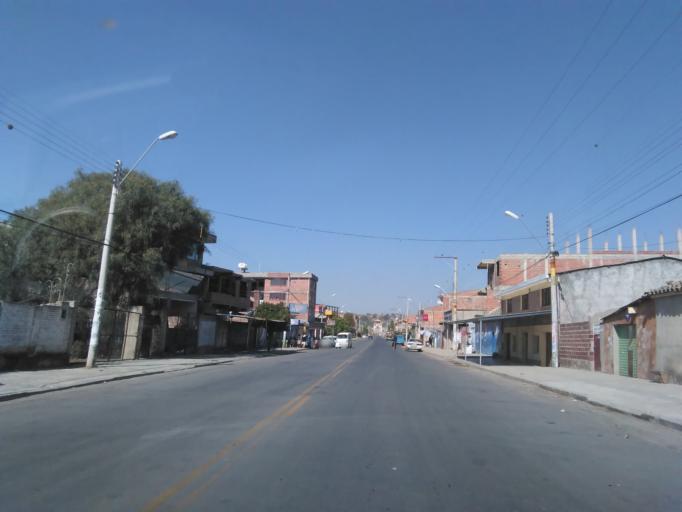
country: BO
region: Cochabamba
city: Sipe Sipe
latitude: -17.4104
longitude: -66.2824
